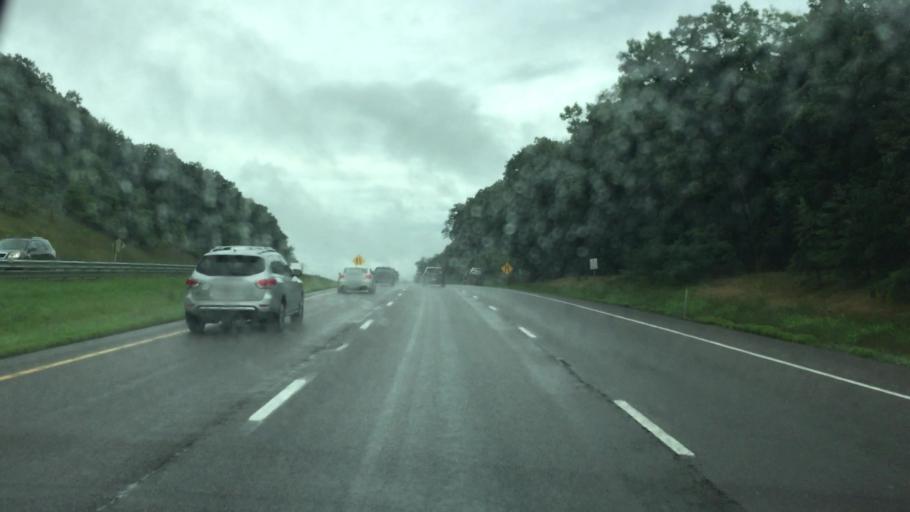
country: US
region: Maryland
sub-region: Washington County
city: Hancock
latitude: 39.7035
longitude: -78.1699
